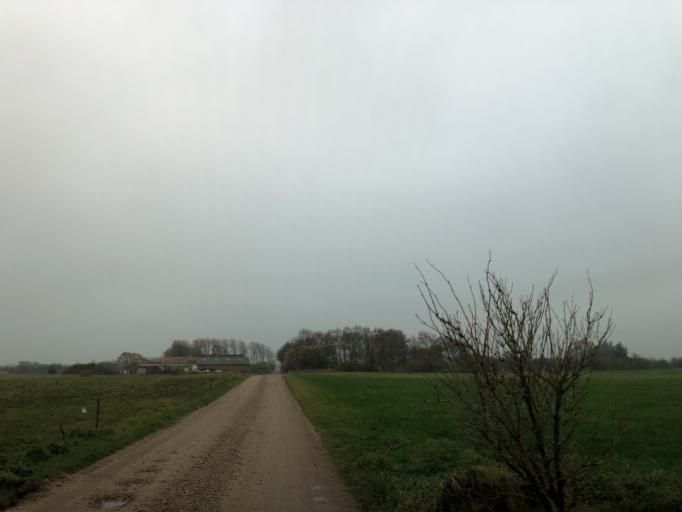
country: DK
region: Central Jutland
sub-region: Herning Kommune
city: Vildbjerg
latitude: 56.2144
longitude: 8.7280
